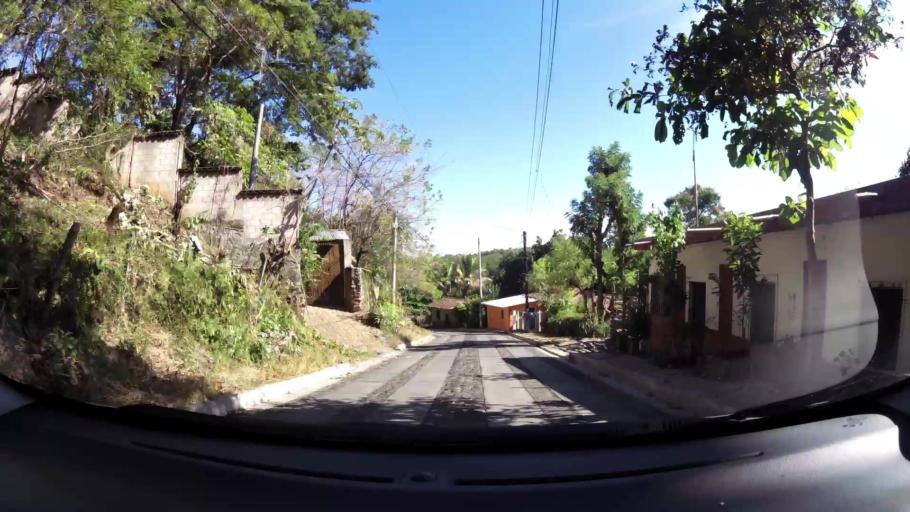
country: SV
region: Cuscatlan
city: Suchitoto
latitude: 13.9409
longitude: -89.0199
